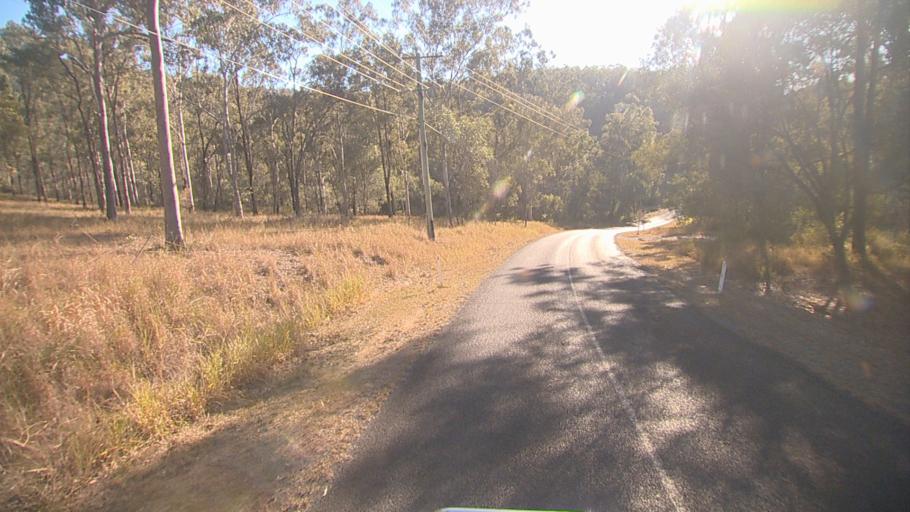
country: AU
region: Queensland
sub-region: Logan
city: Cedar Vale
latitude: -27.8407
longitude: 153.0834
